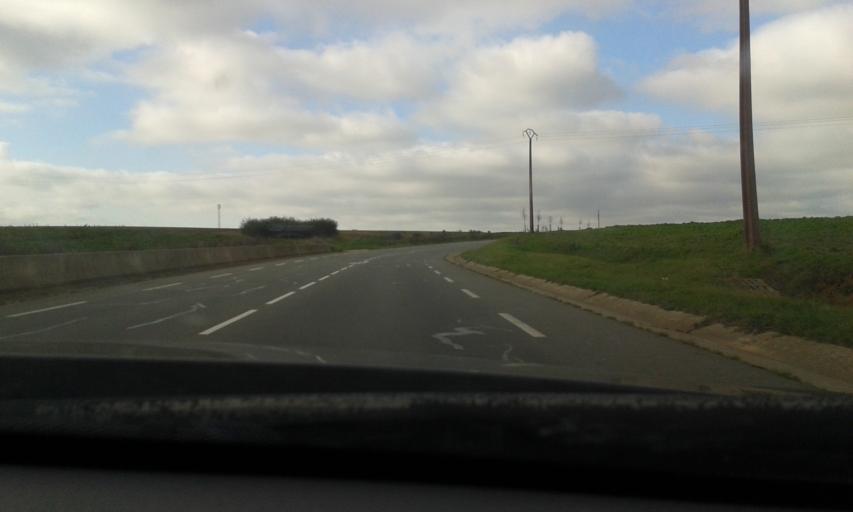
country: FR
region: Nord-Pas-de-Calais
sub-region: Departement du Pas-de-Calais
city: Hames-Boucres
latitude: 50.8696
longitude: 1.8413
